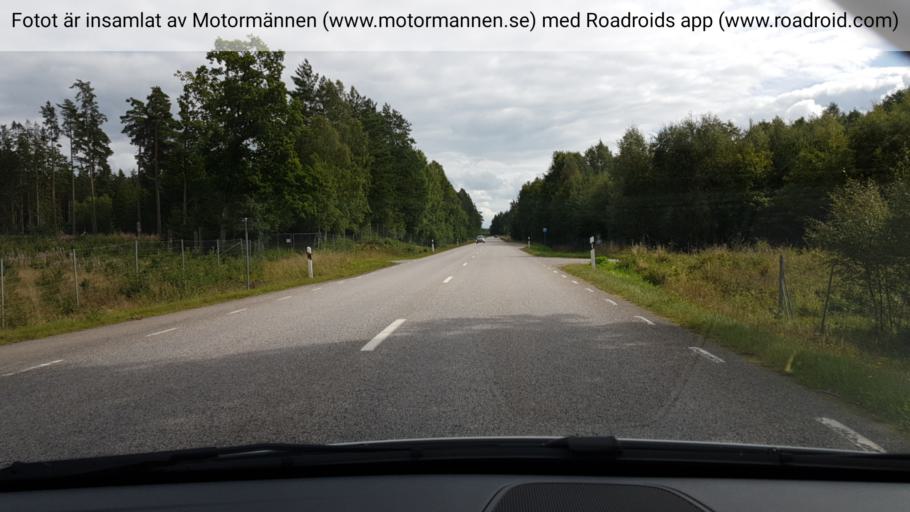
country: SE
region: Vaestra Goetaland
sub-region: Falkopings Kommun
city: Floby
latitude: 58.2005
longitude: 13.3153
